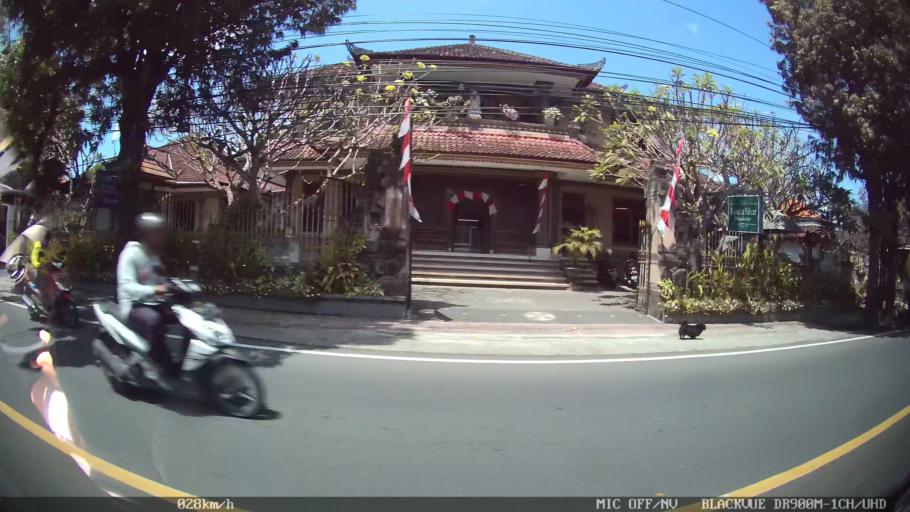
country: ID
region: Bali
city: Banjar Jabejero
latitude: -8.6007
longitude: 115.2687
